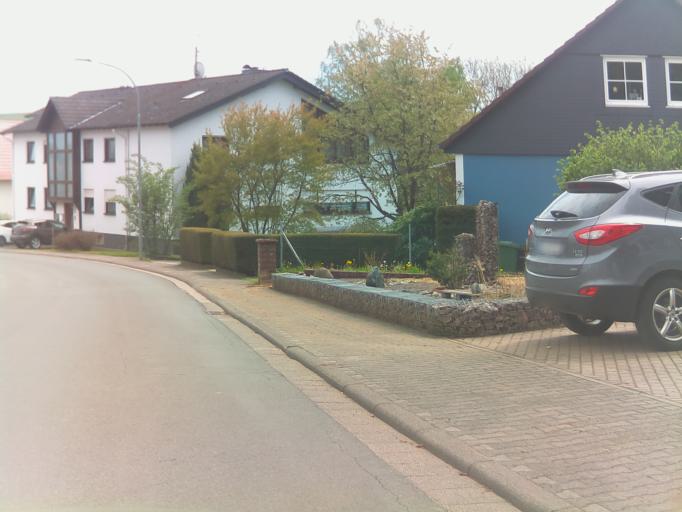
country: DE
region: Hesse
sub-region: Regierungsbezirk Darmstadt
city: Kefenrod
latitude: 50.3276
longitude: 9.1837
